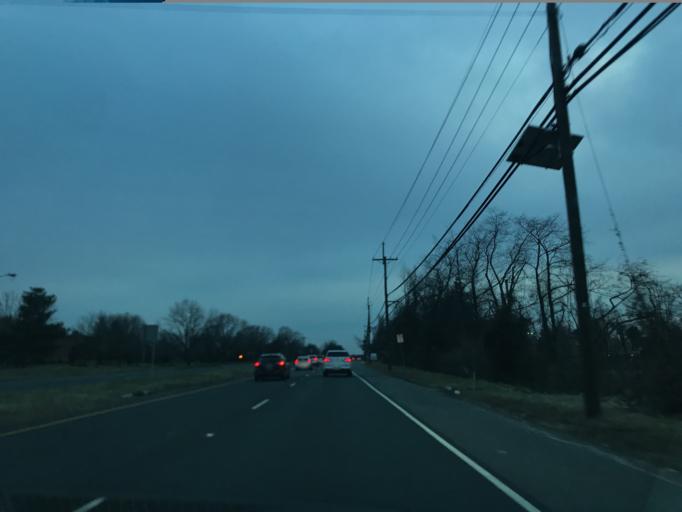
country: US
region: New Jersey
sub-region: Middlesex County
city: Rossmoor
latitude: 40.3463
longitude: -74.4984
